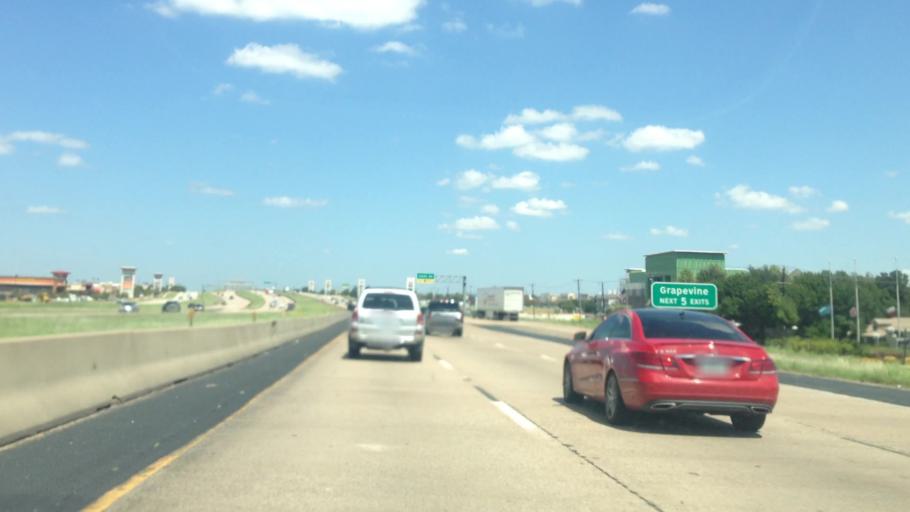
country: US
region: Texas
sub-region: Tarrant County
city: Euless
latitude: 32.8703
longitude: -97.0998
